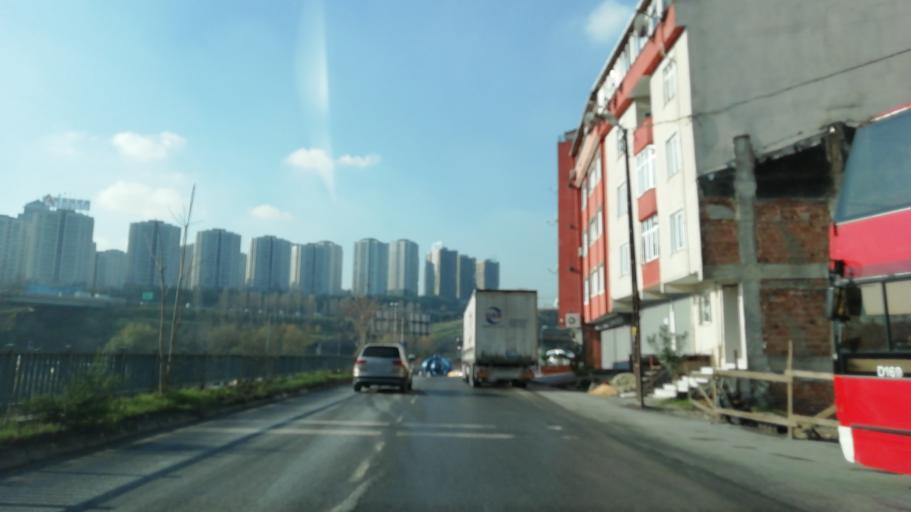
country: TR
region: Istanbul
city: Sultangazi
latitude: 41.0929
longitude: 28.9079
